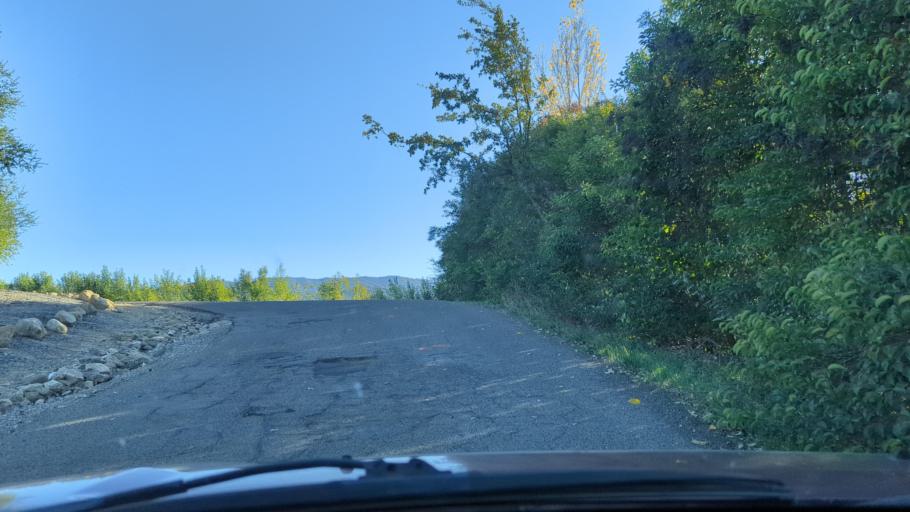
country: US
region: California
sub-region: Santa Barbara County
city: Solvang
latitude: 34.5802
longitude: -120.1021
